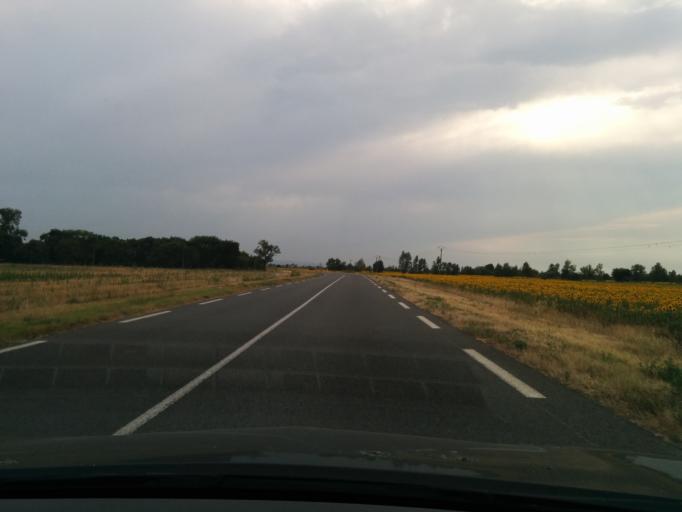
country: FR
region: Languedoc-Roussillon
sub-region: Departement de l'Aude
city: Alzonne
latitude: 43.2611
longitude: 2.2021
